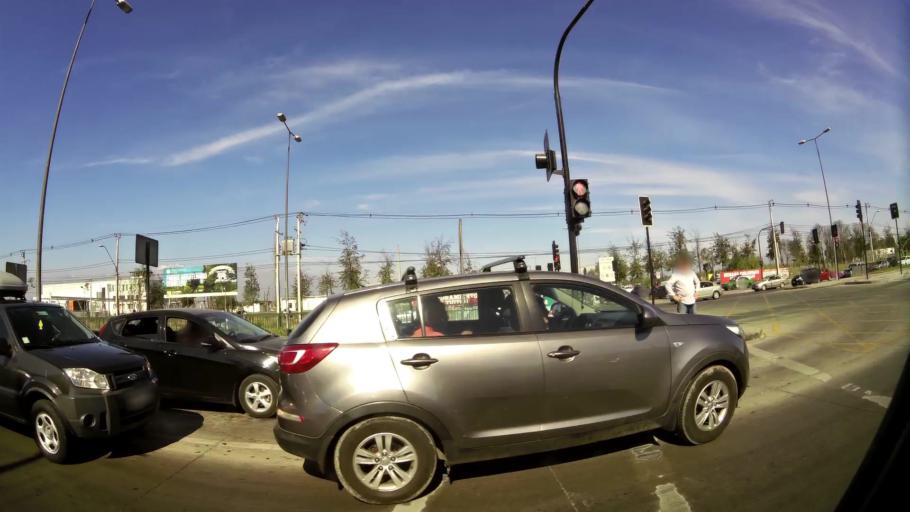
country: CL
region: Santiago Metropolitan
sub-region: Provincia de Santiago
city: Lo Prado
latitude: -33.4954
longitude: -70.7060
